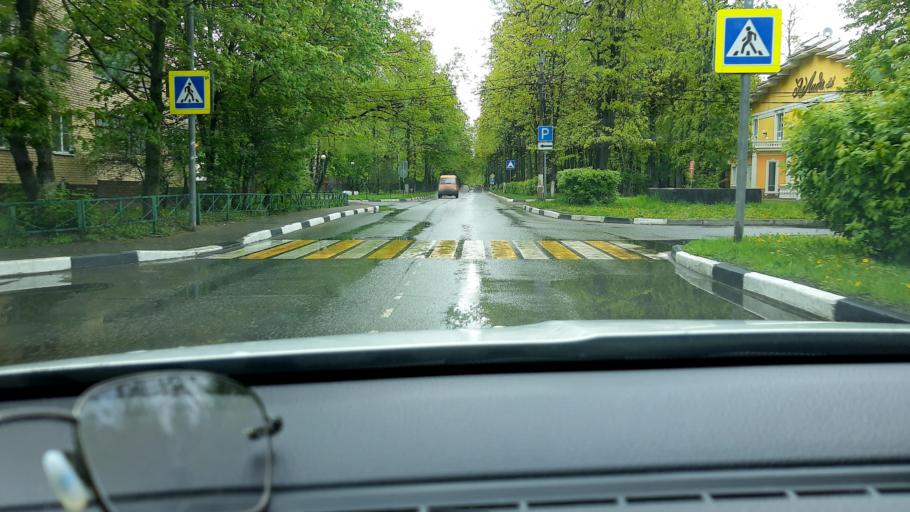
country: RU
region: Moskovskaya
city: Krasnogorsk
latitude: 55.8240
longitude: 37.3328
